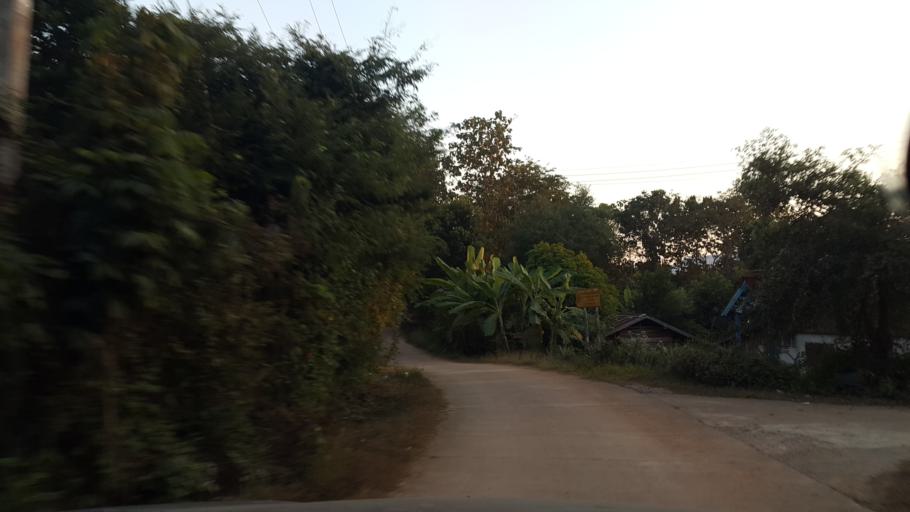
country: TH
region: Phrae
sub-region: Amphoe Wang Chin
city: Wang Chin
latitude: 17.8799
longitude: 99.6232
